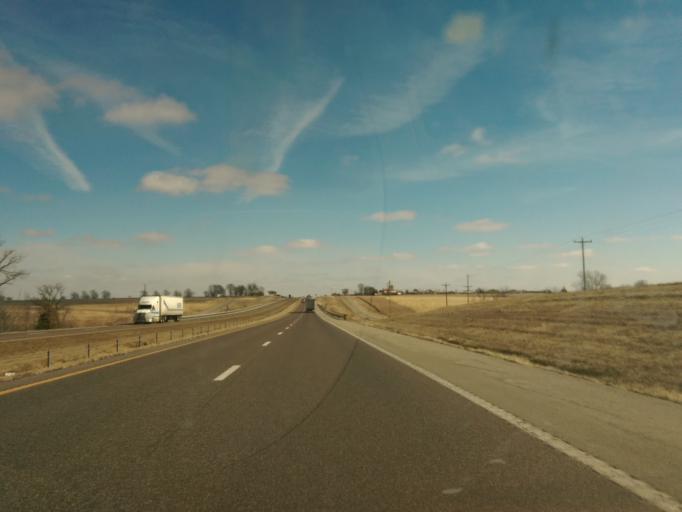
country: US
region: Missouri
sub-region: Callaway County
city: Fulton
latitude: 38.9439
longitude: -91.9117
